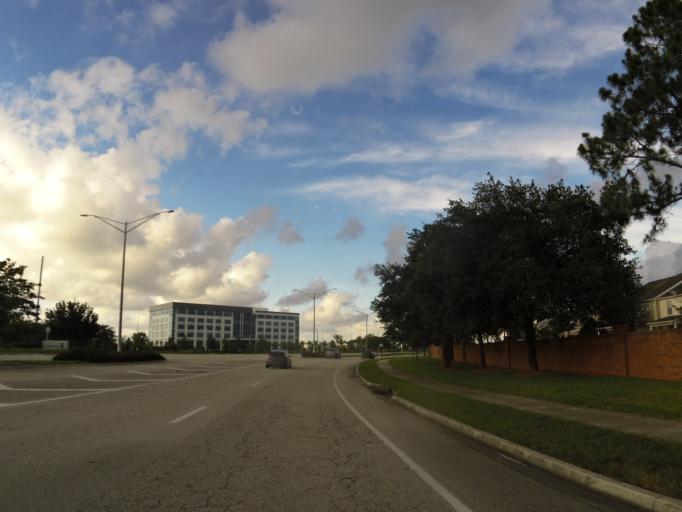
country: US
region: Florida
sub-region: Saint Johns County
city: Ponte Vedra Beach
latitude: 30.2463
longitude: -81.5282
